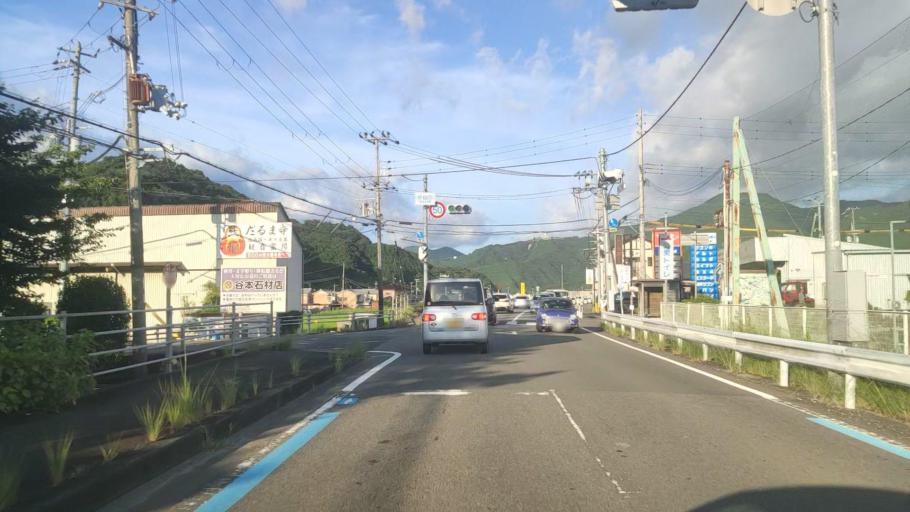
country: JP
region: Wakayama
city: Tanabe
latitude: 33.7158
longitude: 135.4604
